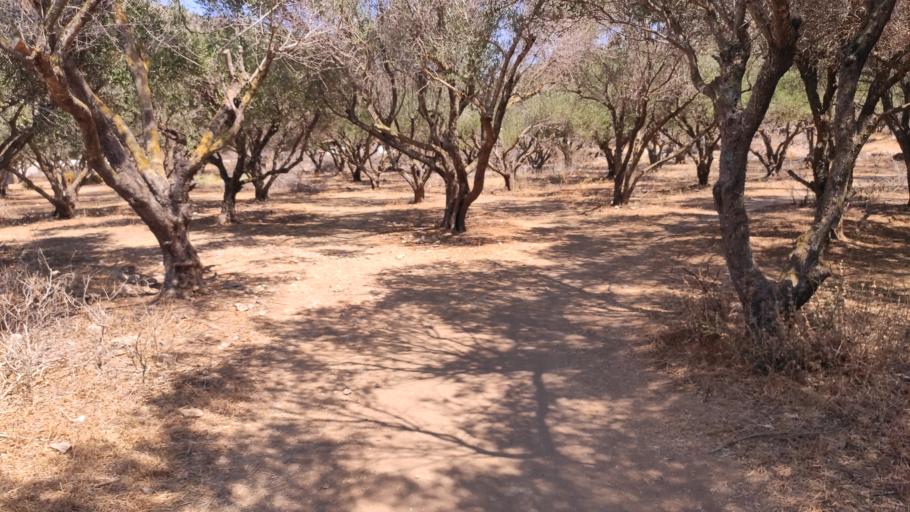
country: GR
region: South Aegean
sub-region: Nomos Dodekanisou
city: Pylion
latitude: 36.9333
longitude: 27.1356
